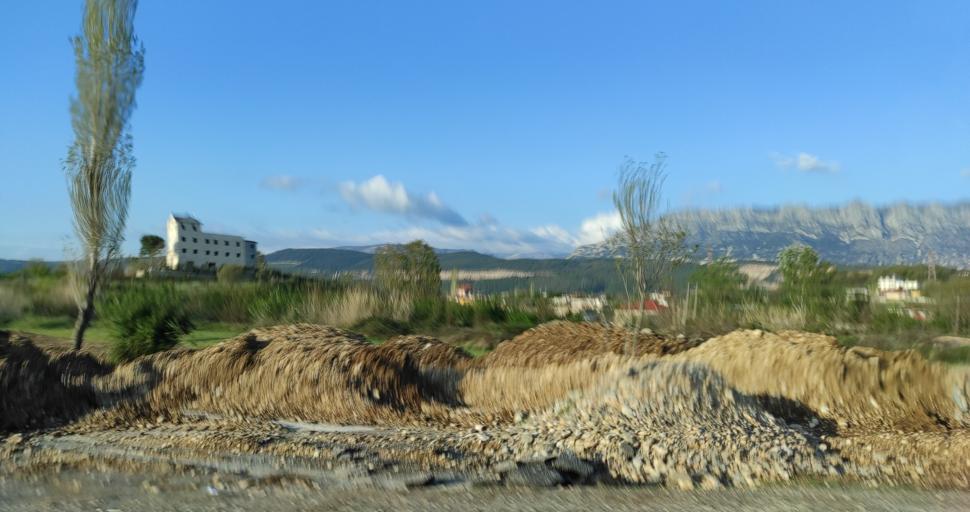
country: AL
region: Durres
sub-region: Rrethi i Krujes
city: Fushe-Kruje
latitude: 41.4844
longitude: 19.7318
